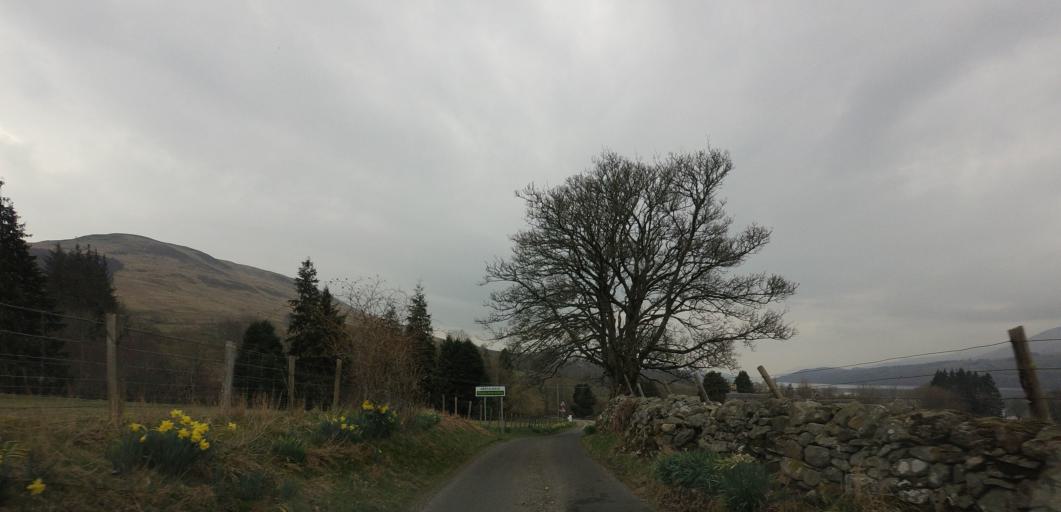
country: GB
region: Scotland
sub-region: Perth and Kinross
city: Comrie
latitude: 56.5286
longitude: -4.1107
